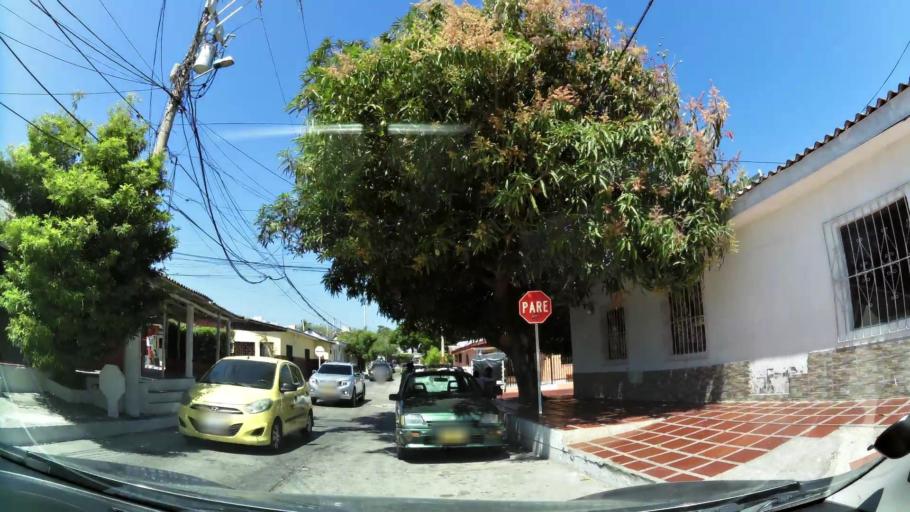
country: CO
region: Atlantico
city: Barranquilla
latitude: 11.0067
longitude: -74.7908
